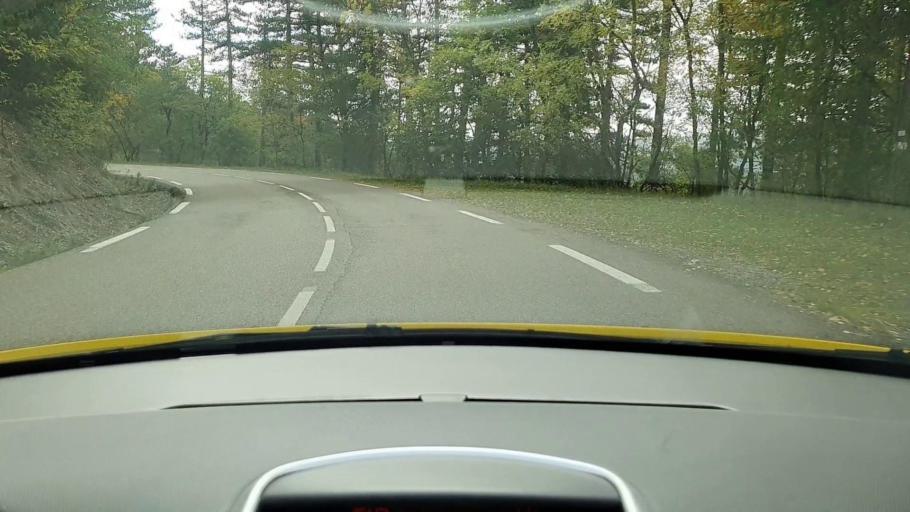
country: FR
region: Languedoc-Roussillon
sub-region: Departement de la Lozere
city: Meyrueis
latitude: 44.1256
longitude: 3.4457
